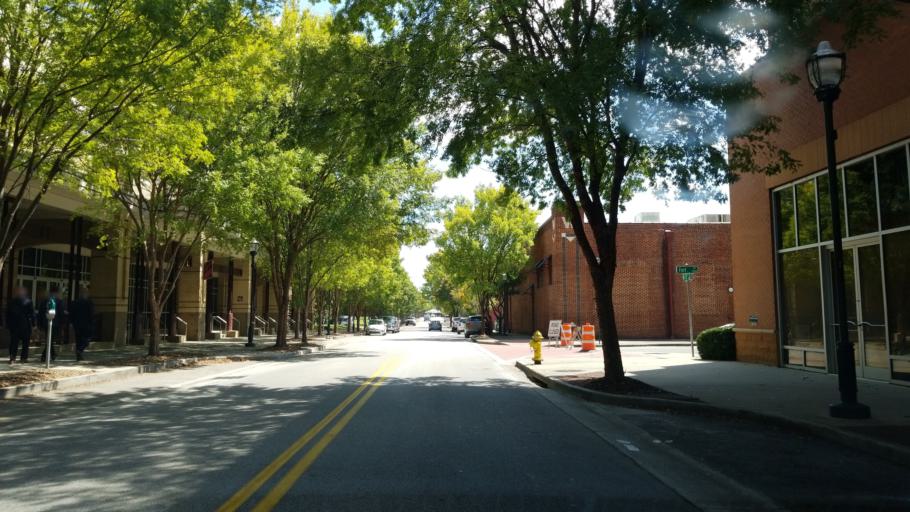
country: US
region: Tennessee
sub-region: Hamilton County
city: Chattanooga
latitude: 35.0413
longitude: -85.3138
